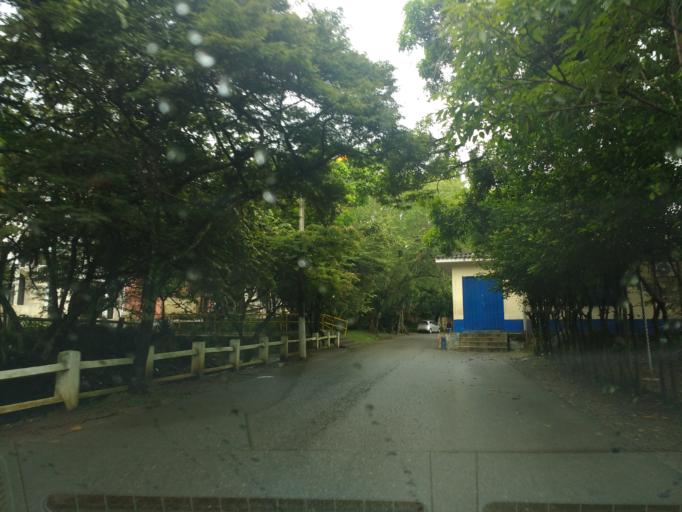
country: CO
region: Cauca
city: Santander de Quilichao
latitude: 3.0033
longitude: -76.4804
